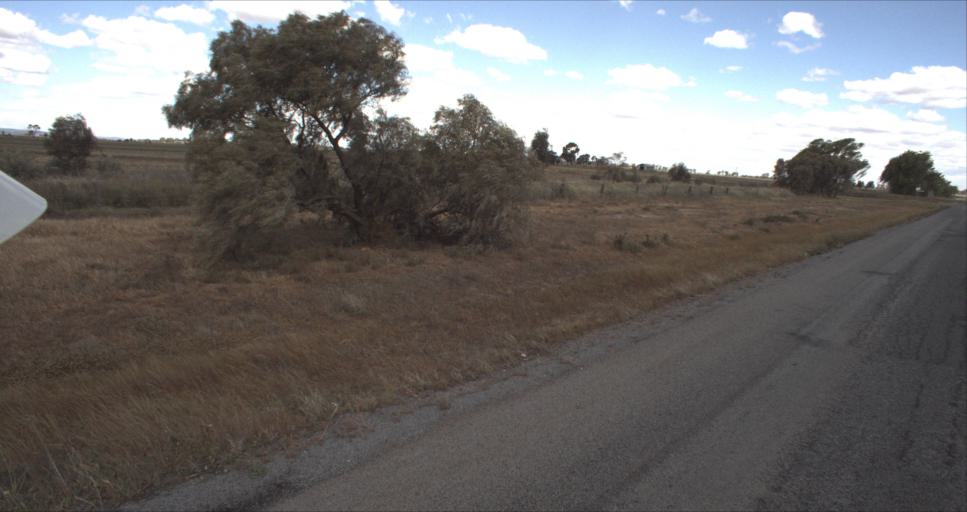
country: AU
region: New South Wales
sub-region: Leeton
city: Leeton
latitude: -34.4432
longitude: 146.2560
